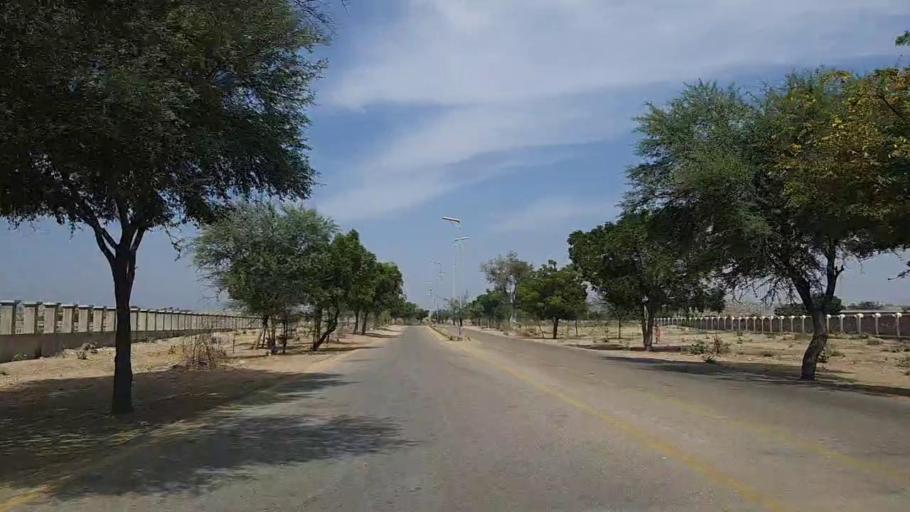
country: PK
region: Sindh
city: Mithi
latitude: 24.7511
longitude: 69.7953
